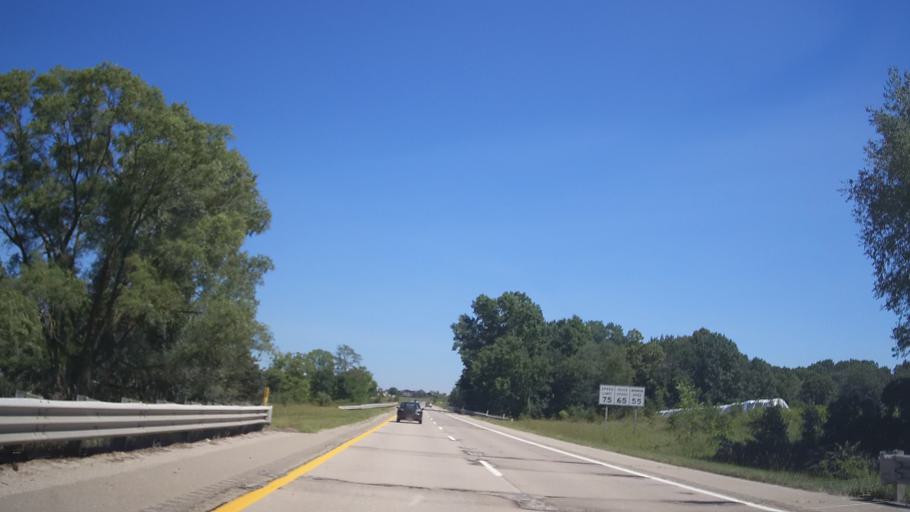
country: US
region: Michigan
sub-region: Clare County
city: Clare
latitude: 43.8227
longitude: -84.7447
